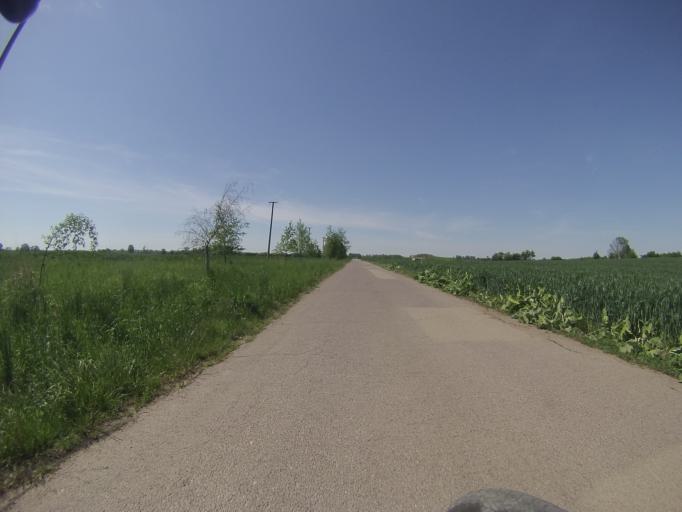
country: CZ
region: South Moravian
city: Novosedly
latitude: 48.8132
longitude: 16.4797
